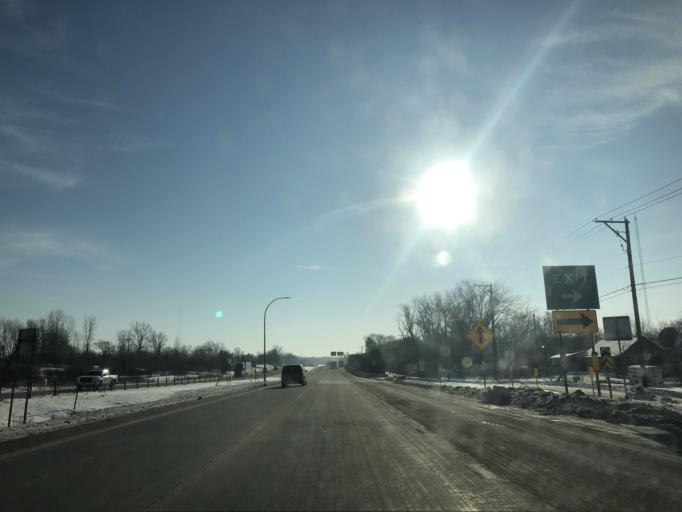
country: US
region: Minnesota
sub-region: Ramsey County
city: New Brighton
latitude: 45.0844
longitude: -93.1826
